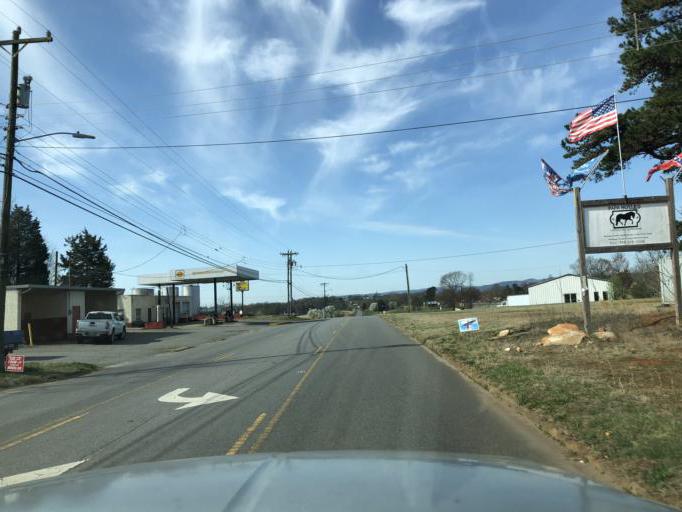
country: US
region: North Carolina
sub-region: Burke County
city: Salem
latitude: 35.5093
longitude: -81.6214
